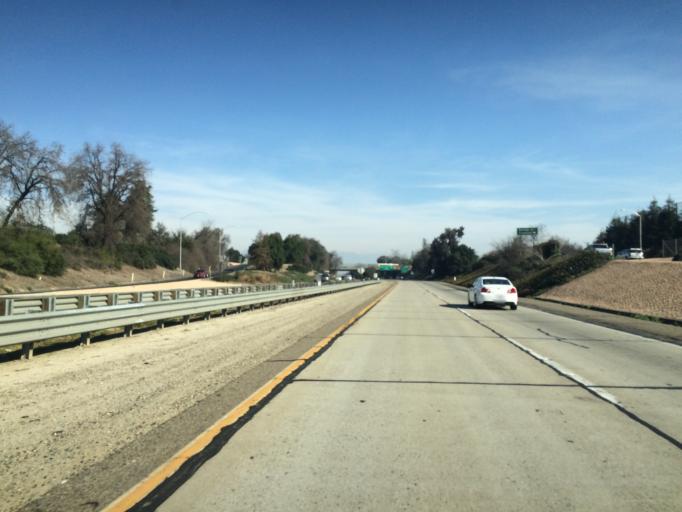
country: US
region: California
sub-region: Tulare County
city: Visalia
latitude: 36.3272
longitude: -119.3179
